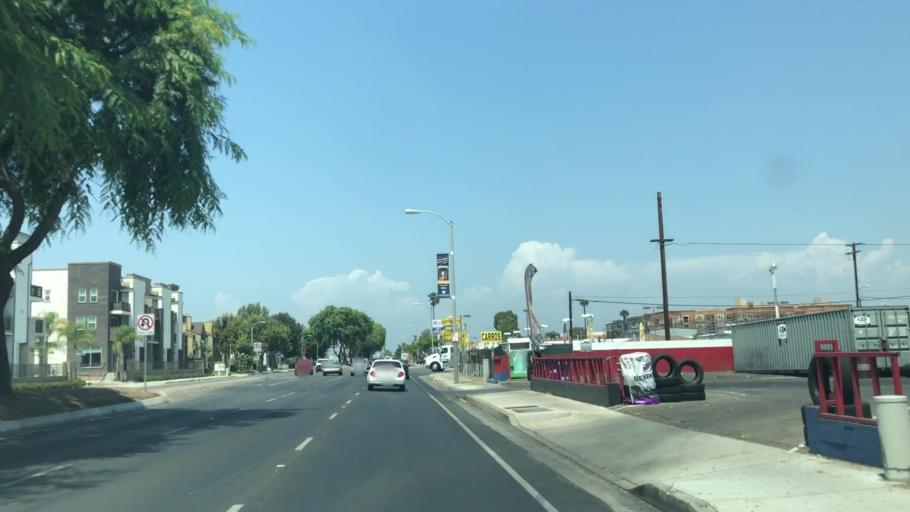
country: US
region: California
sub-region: Orange County
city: Garden Grove
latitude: 33.7554
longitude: -117.9201
